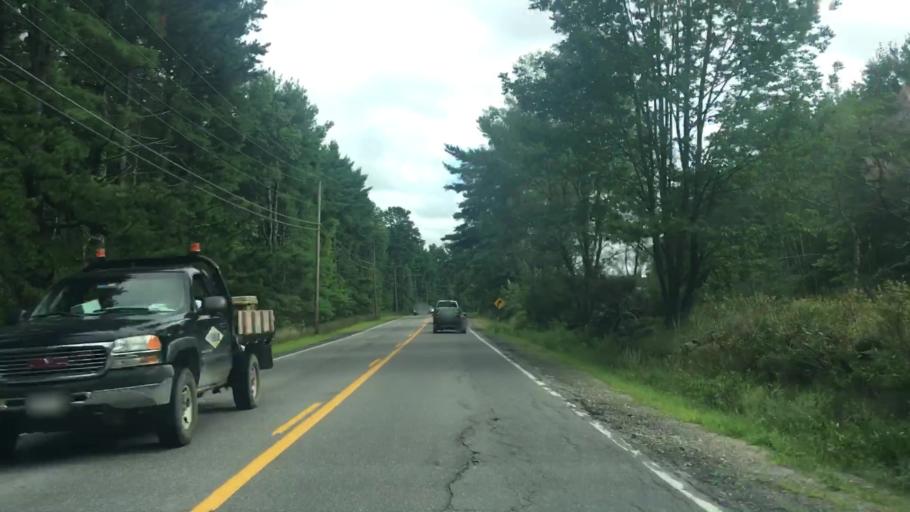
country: US
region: Maine
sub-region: York County
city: Lake Arrowhead
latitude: 43.6111
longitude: -70.7172
